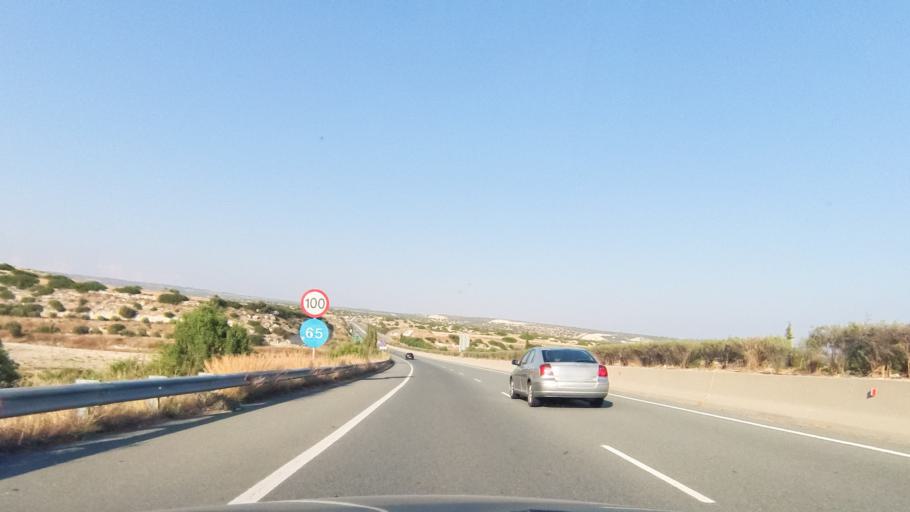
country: CY
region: Limassol
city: Pissouri
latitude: 34.6826
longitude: 32.7666
